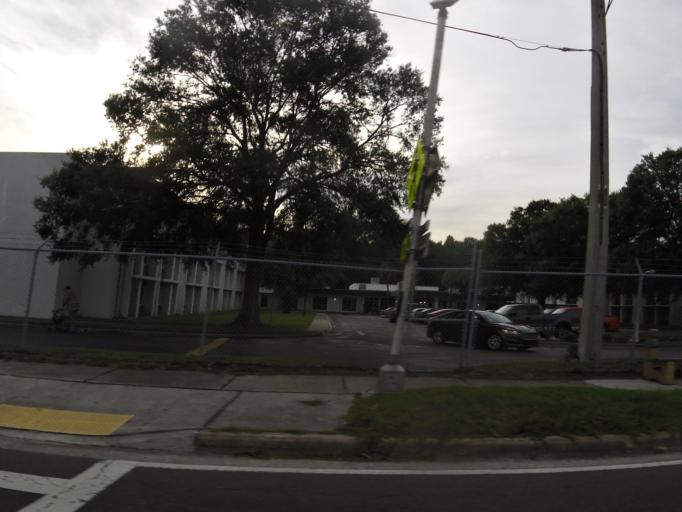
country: US
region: Florida
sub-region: Duval County
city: Jacksonville
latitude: 30.4031
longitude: -81.7214
